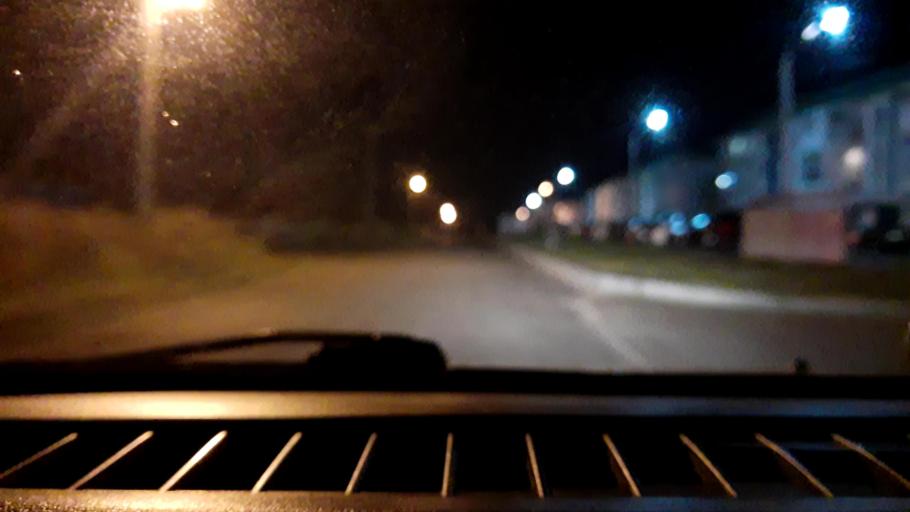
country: RU
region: Nizjnij Novgorod
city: Burevestnik
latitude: 56.1927
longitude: 43.8605
